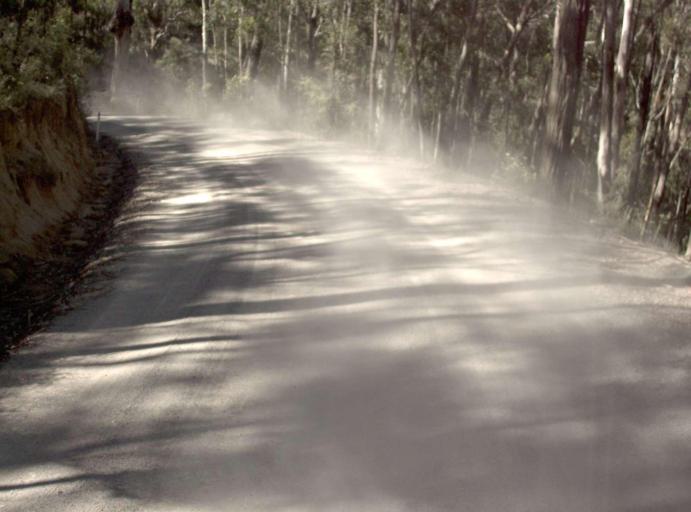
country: AU
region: New South Wales
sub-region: Bombala
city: Bombala
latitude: -37.2642
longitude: 148.7274
